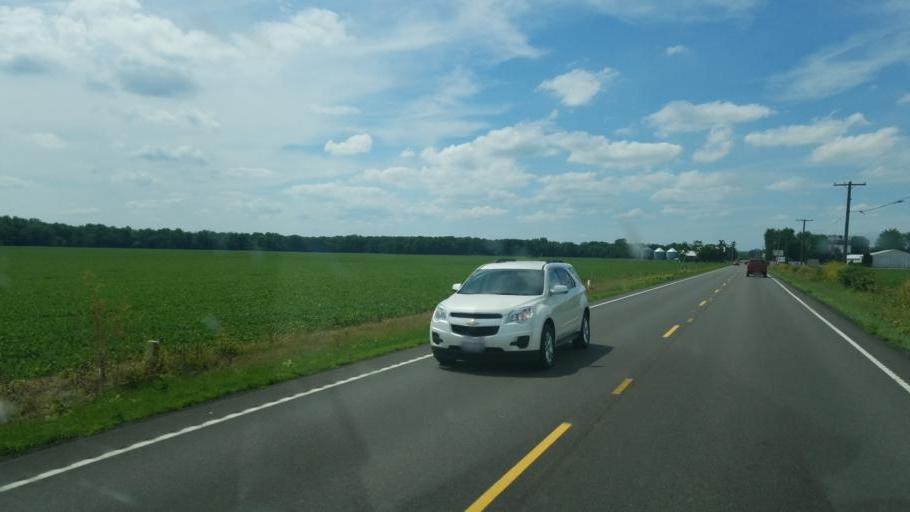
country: US
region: Ohio
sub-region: Knox County
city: Fredericktown
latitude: 40.4475
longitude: -82.5340
